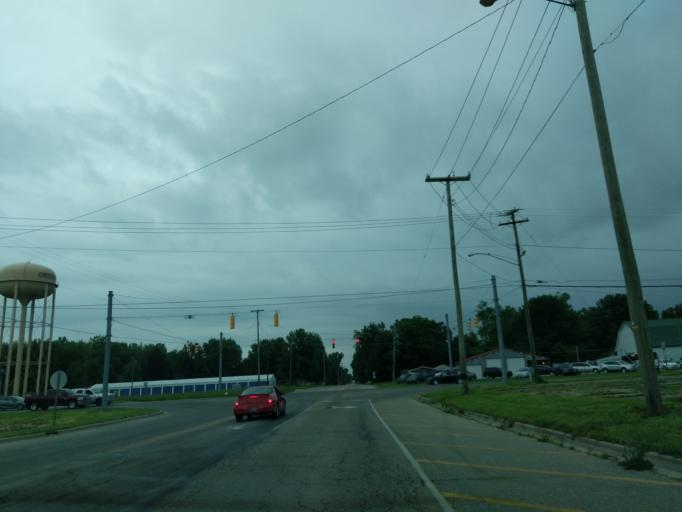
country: US
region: Indiana
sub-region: Delaware County
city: Daleville
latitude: 40.1146
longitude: -85.5761
